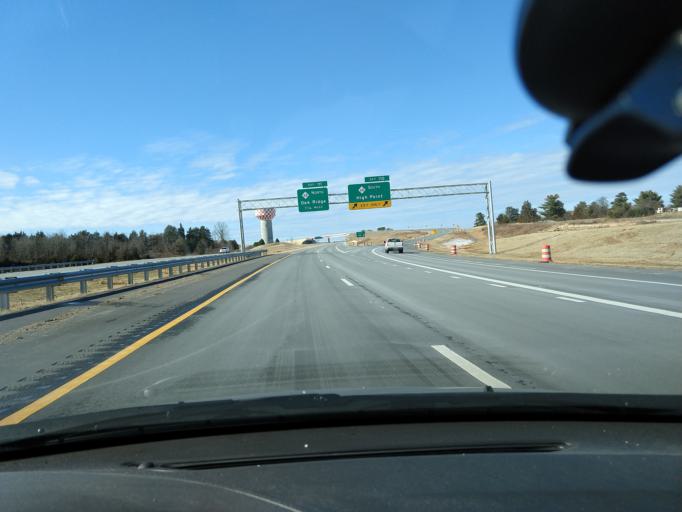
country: US
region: North Carolina
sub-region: Guilford County
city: Oak Ridge
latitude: 36.1208
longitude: -79.9529
